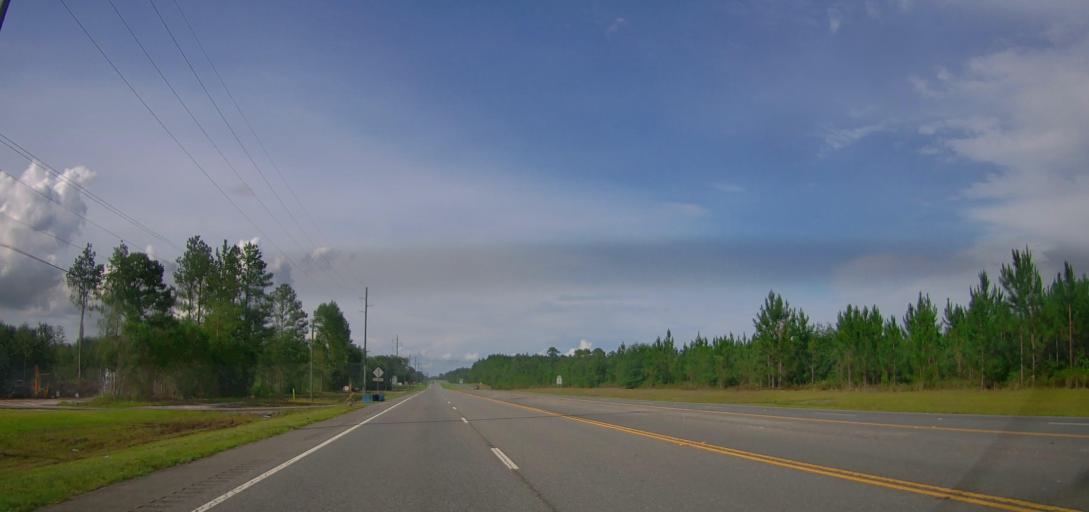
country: US
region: Georgia
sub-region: Wayne County
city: Jesup
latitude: 31.5120
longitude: -81.9957
